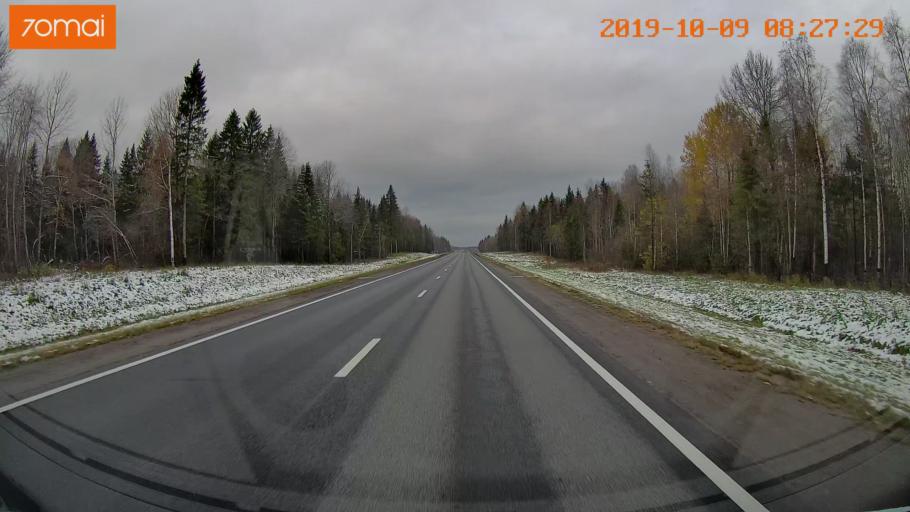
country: RU
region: Vologda
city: Gryazovets
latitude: 58.8044
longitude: 40.2479
